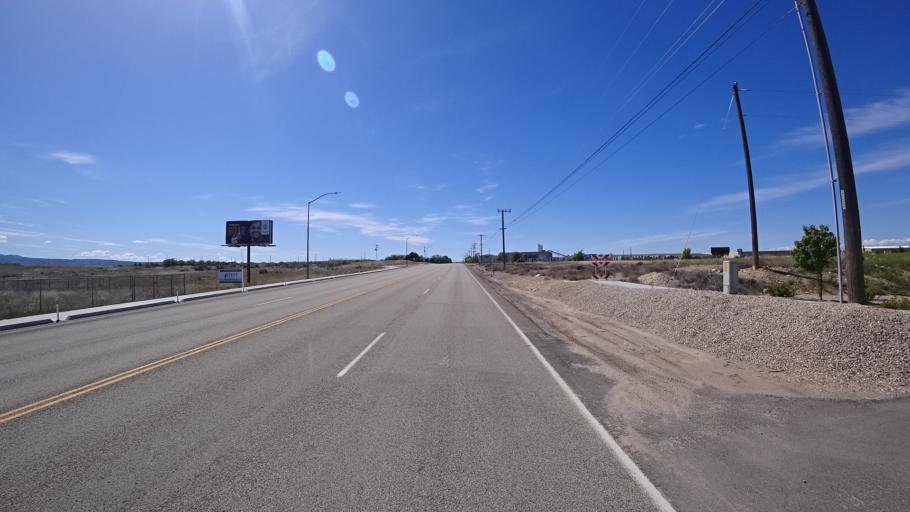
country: US
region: Idaho
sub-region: Ada County
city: Boise
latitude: 43.5372
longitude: -116.1541
